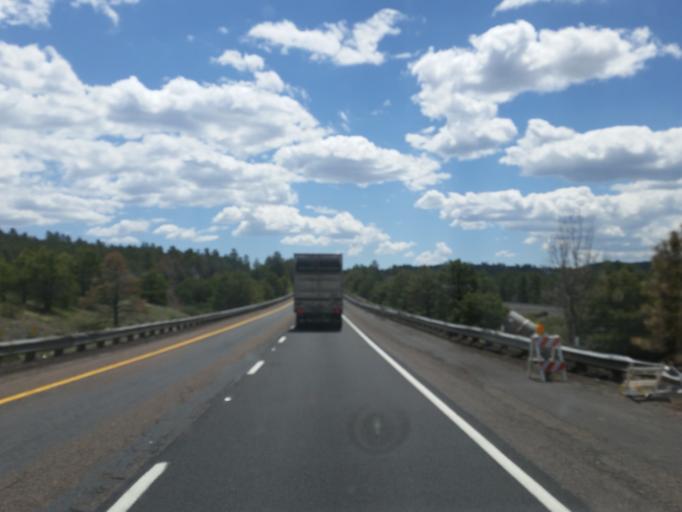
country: US
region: Arizona
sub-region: Coconino County
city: Parks
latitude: 35.2554
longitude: -111.9211
